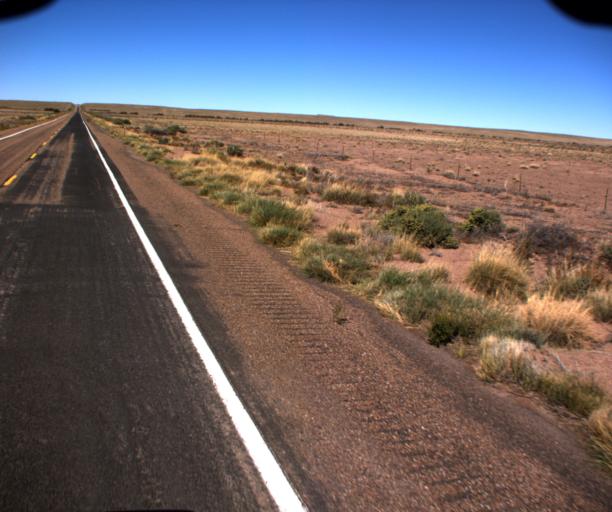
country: US
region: Arizona
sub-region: Navajo County
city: Snowflake
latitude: 34.7358
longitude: -109.7874
